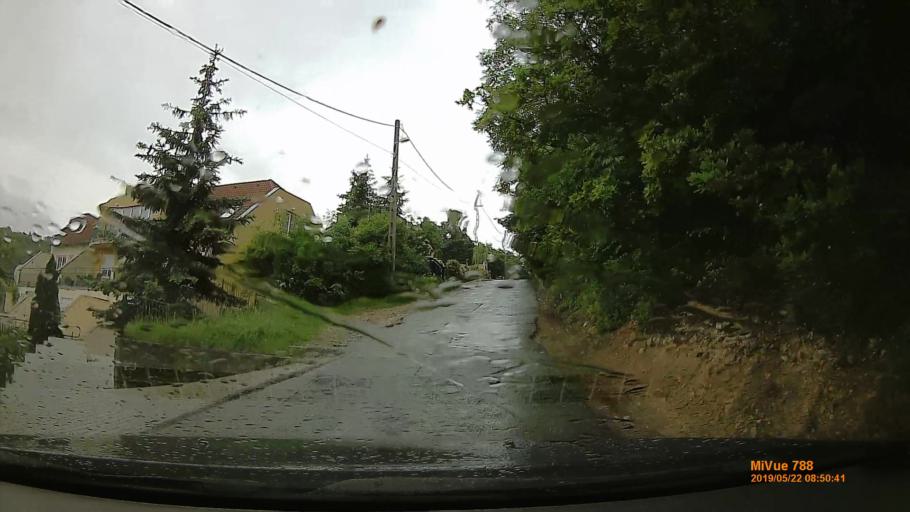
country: HU
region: Budapest
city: Budapest III. keruelet
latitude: 47.5386
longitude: 19.0184
